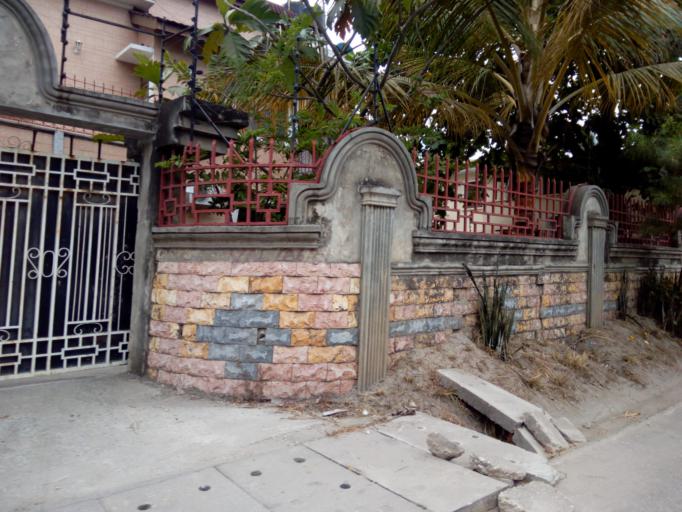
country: TZ
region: Zanzibar Urban/West
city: Zanzibar
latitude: -6.1842
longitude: 39.2057
